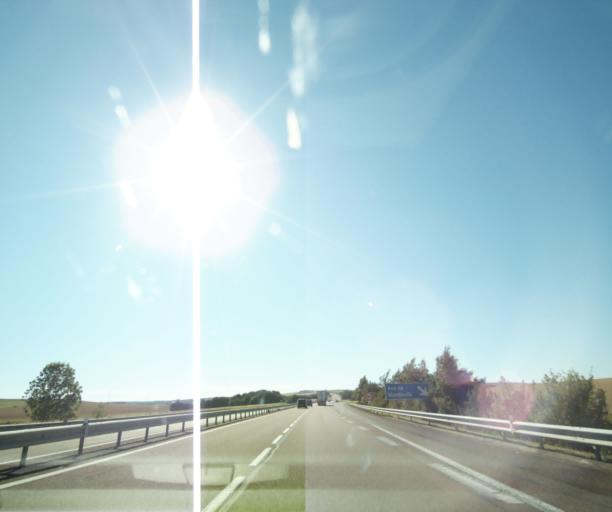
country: FR
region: Champagne-Ardenne
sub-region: Departement de l'Aube
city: Bar-sur-Aube
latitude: 48.1365
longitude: 4.6446
